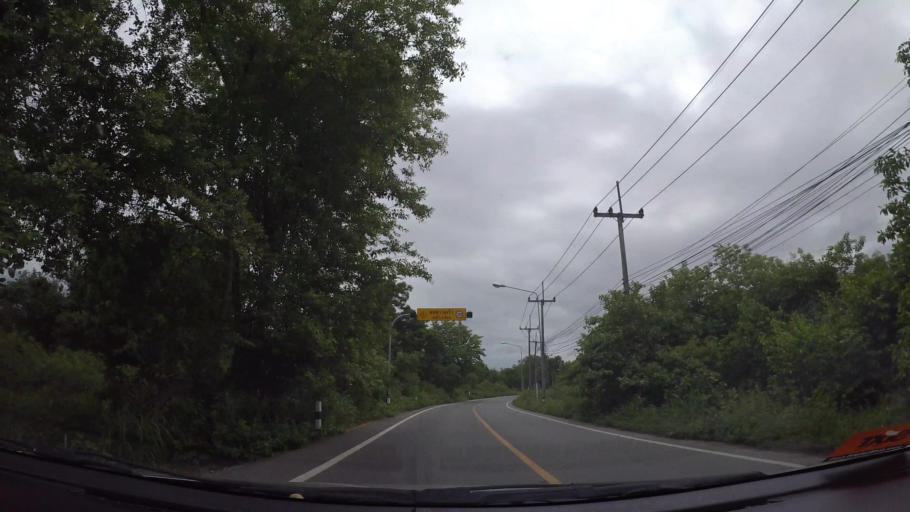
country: TH
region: Chon Buri
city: Si Racha
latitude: 13.1835
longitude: 100.9752
